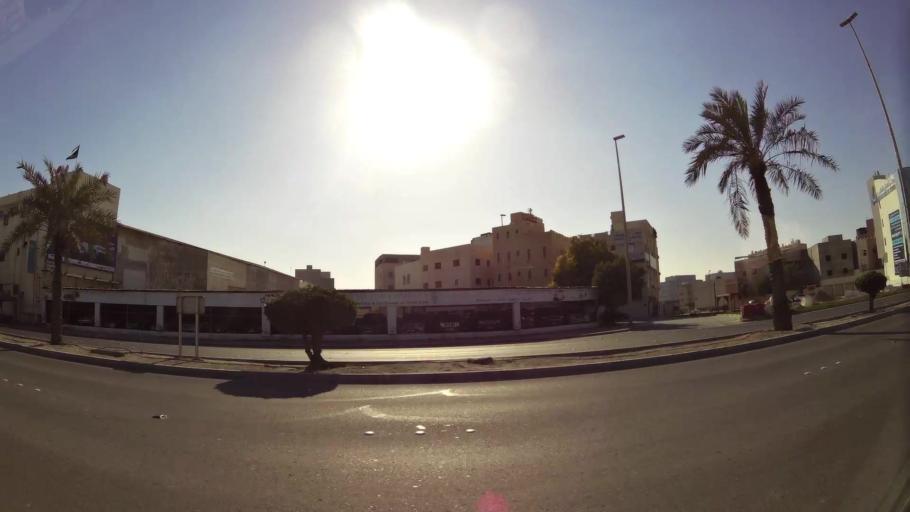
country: BH
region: Manama
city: Manama
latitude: 26.2145
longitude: 50.5656
